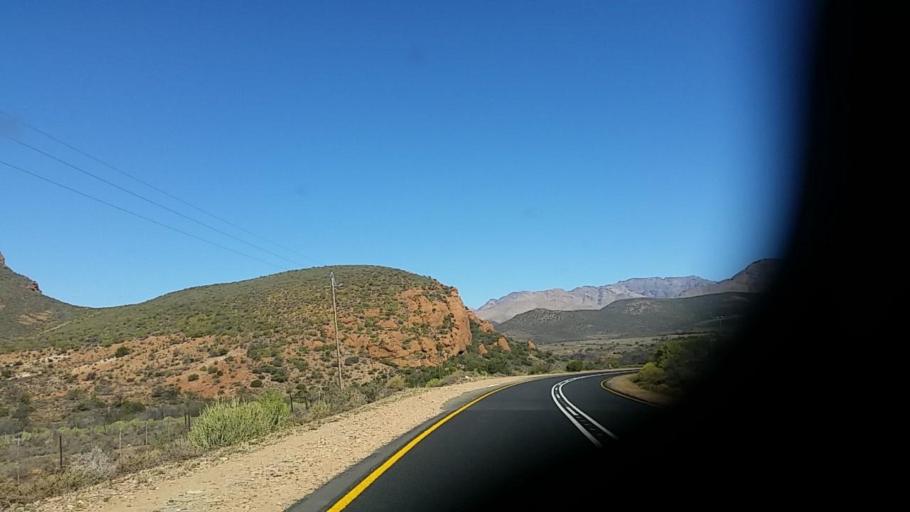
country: ZA
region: Western Cape
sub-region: Eden District Municipality
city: George
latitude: -33.5300
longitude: 22.7157
